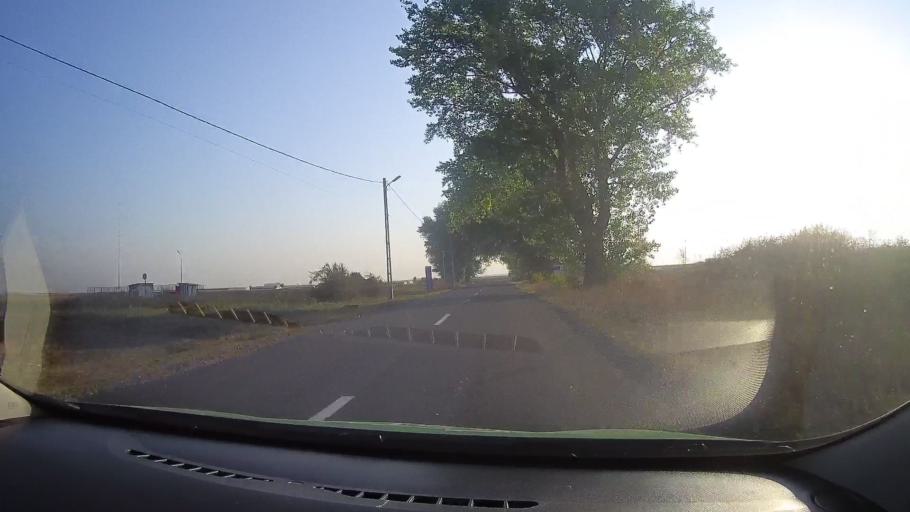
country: RO
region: Arad
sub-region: Comuna Curtici
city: Curtici
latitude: 46.3488
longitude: 21.3317
